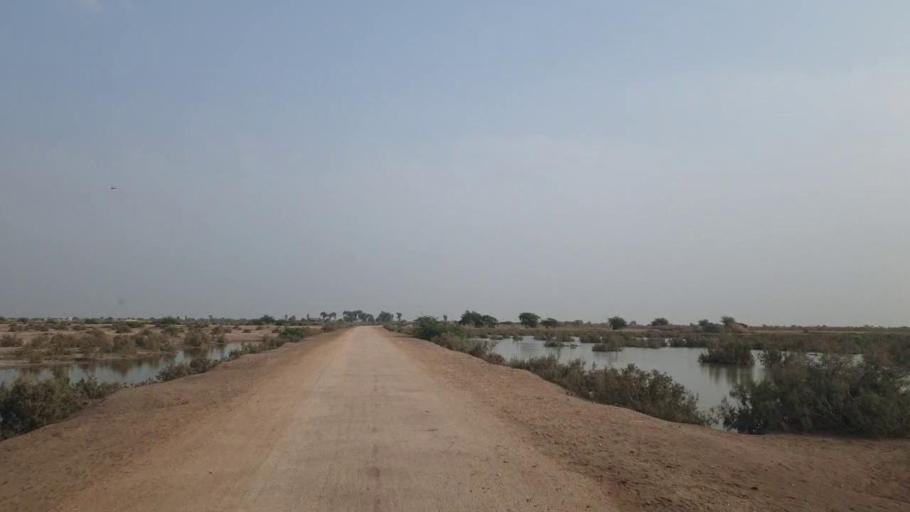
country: PK
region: Sindh
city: Badin
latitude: 24.6060
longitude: 68.6913
